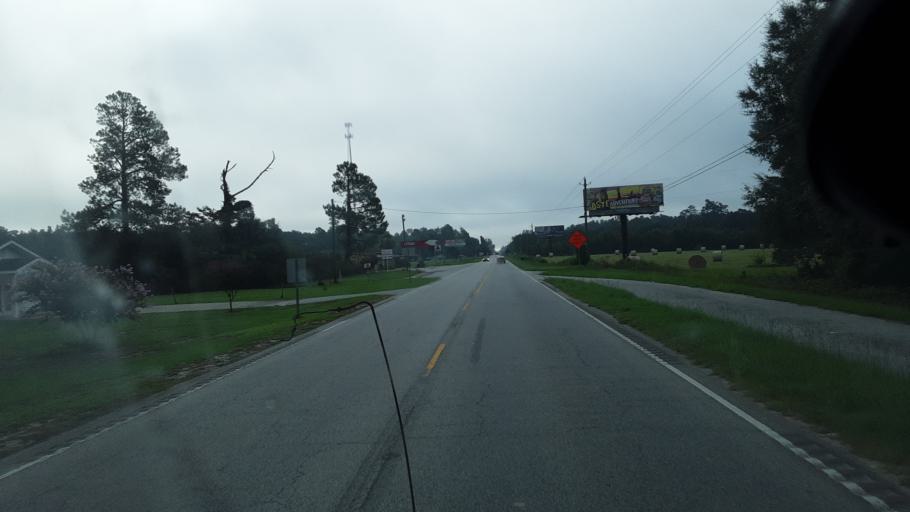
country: US
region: South Carolina
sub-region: Florence County
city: Johnsonville
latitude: 33.8666
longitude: -79.3356
